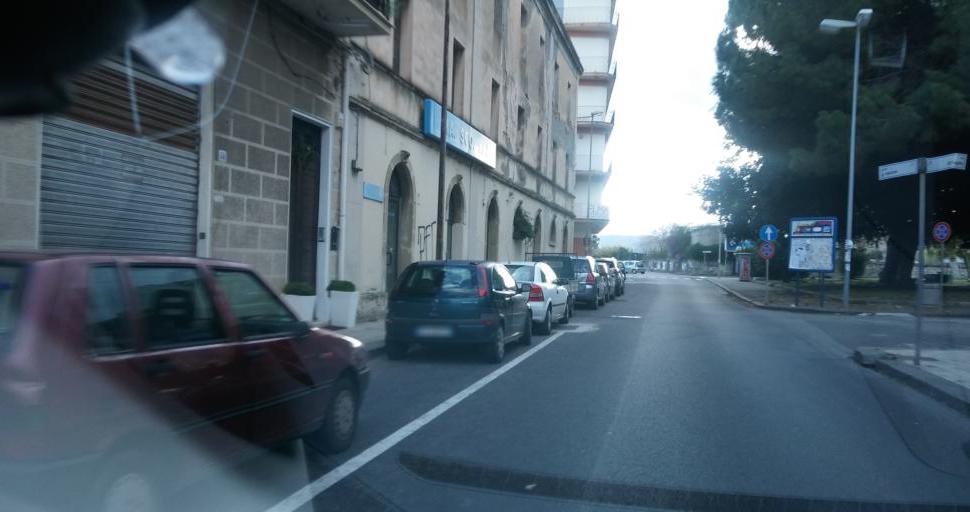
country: IT
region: Sicily
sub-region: Messina
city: Milazzo
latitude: 38.2131
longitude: 15.2444
